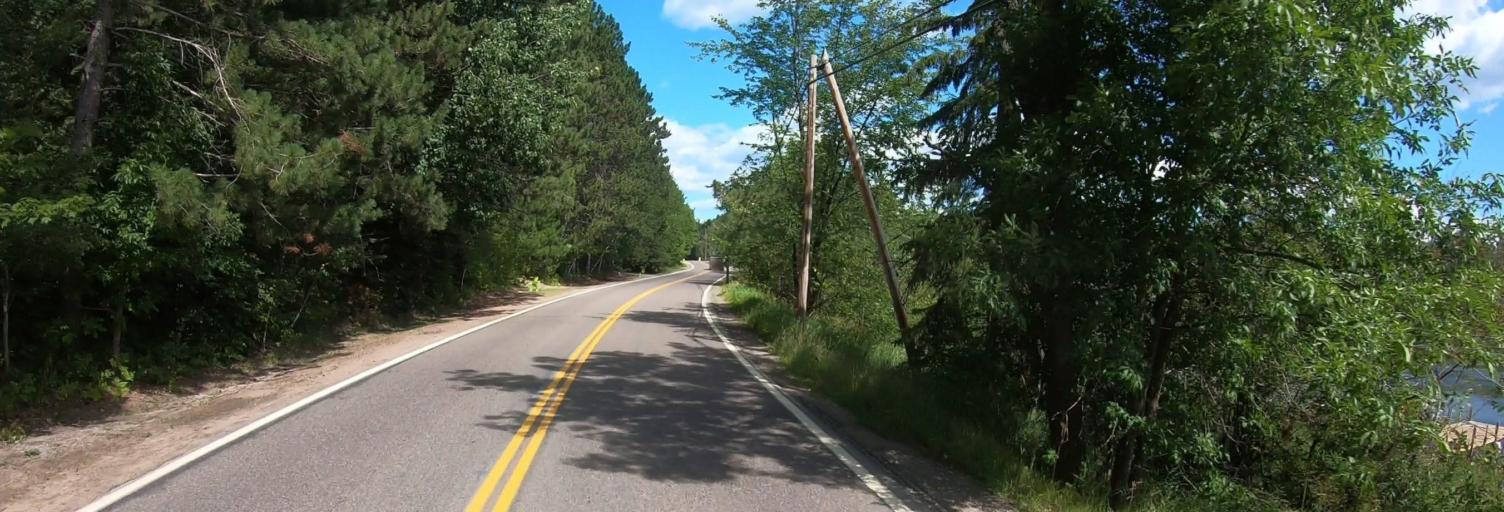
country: US
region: Minnesota
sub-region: Saint Louis County
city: Mountain Iron
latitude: 47.9446
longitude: -92.6647
